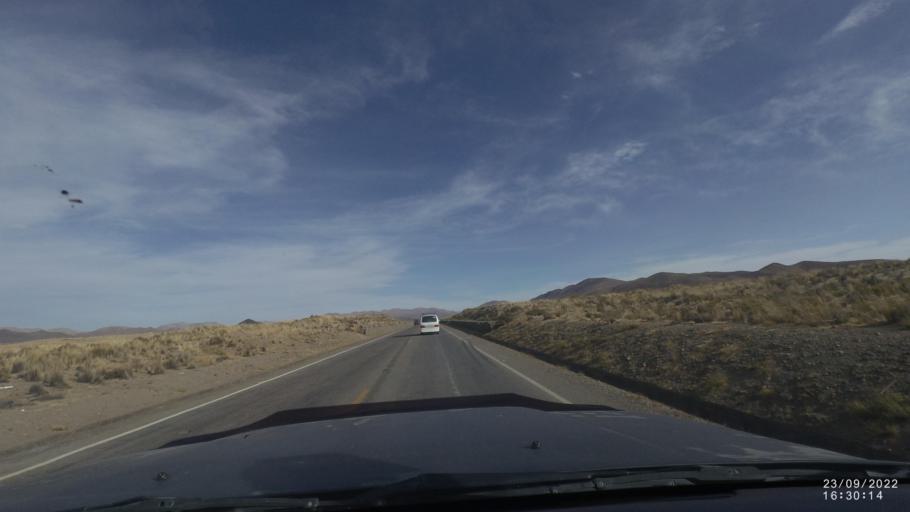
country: BO
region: Oruro
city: Machacamarca
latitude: -18.1517
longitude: -66.9882
